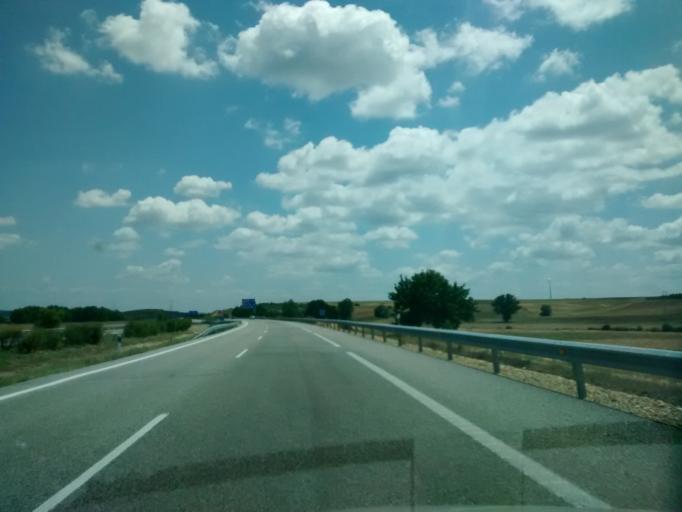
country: ES
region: Castille and Leon
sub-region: Provincia de Leon
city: Astorga
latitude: 42.4403
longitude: -6.0671
